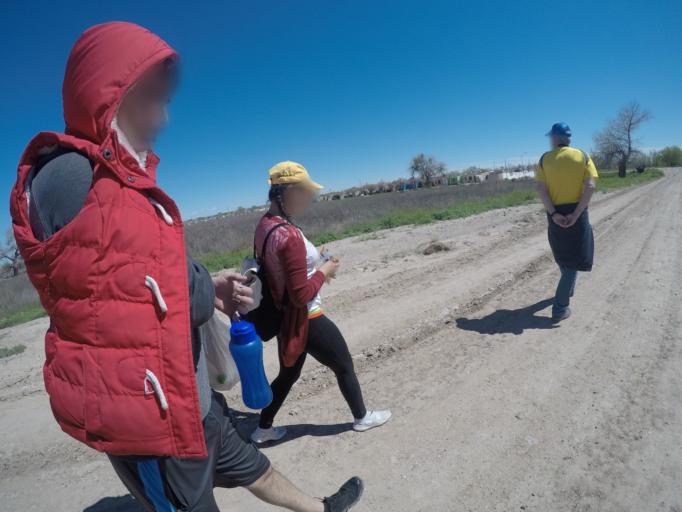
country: US
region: Texas
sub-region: El Paso County
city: Socorro Mission Number 1 Colonia
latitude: 31.6124
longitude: -106.3156
